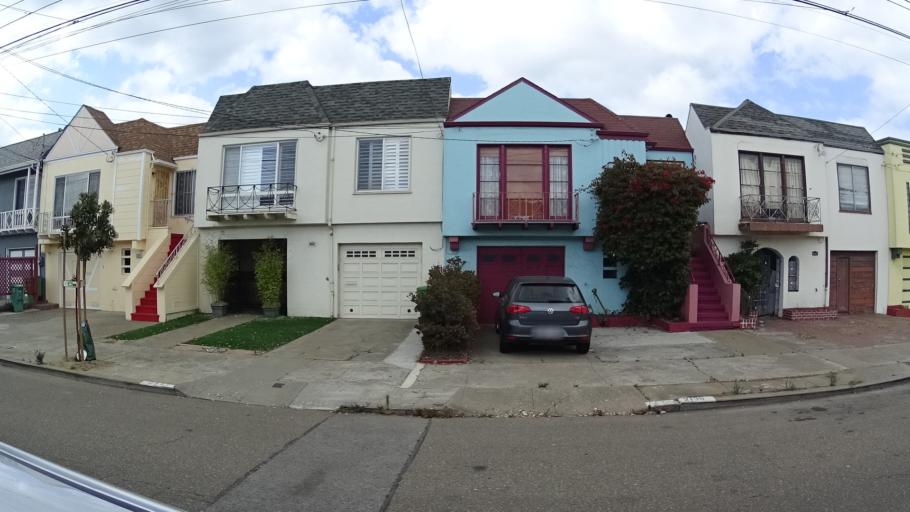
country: US
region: California
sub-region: San Mateo County
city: Daly City
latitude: 37.7465
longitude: -122.5049
